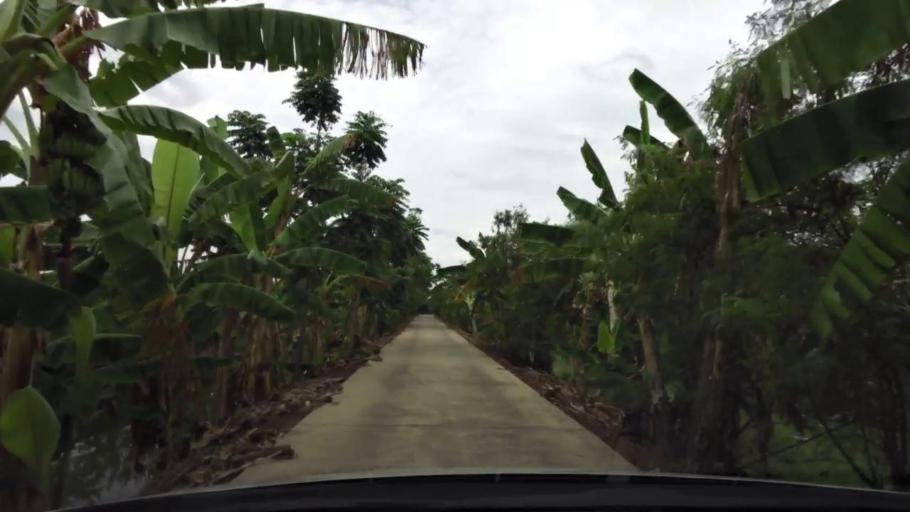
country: TH
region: Ratchaburi
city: Damnoen Saduak
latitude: 13.5514
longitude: 99.9997
